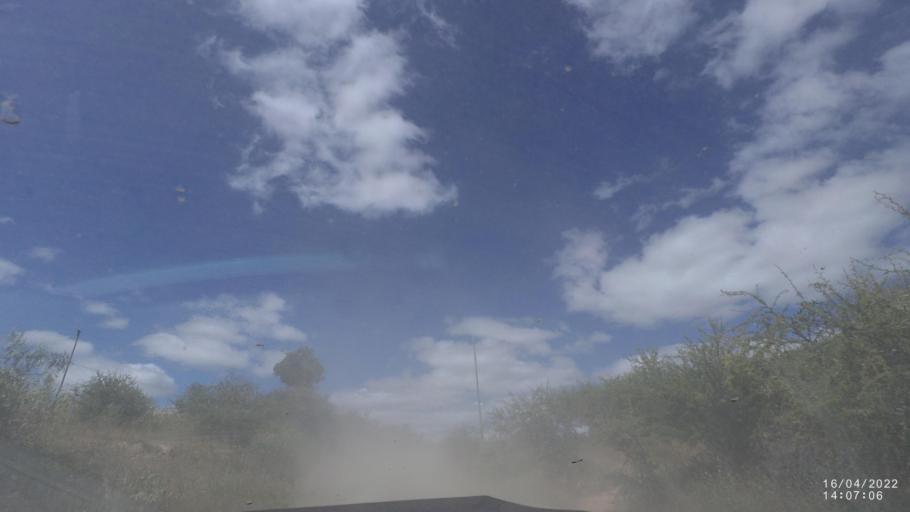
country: BO
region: Cochabamba
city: Mizque
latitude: -18.0576
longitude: -65.5276
